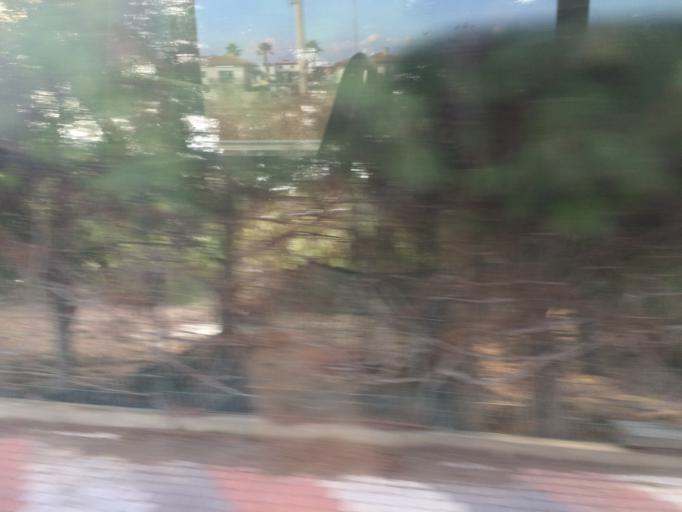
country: TR
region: Izmir
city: Menemen
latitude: 38.5026
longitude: 26.9594
